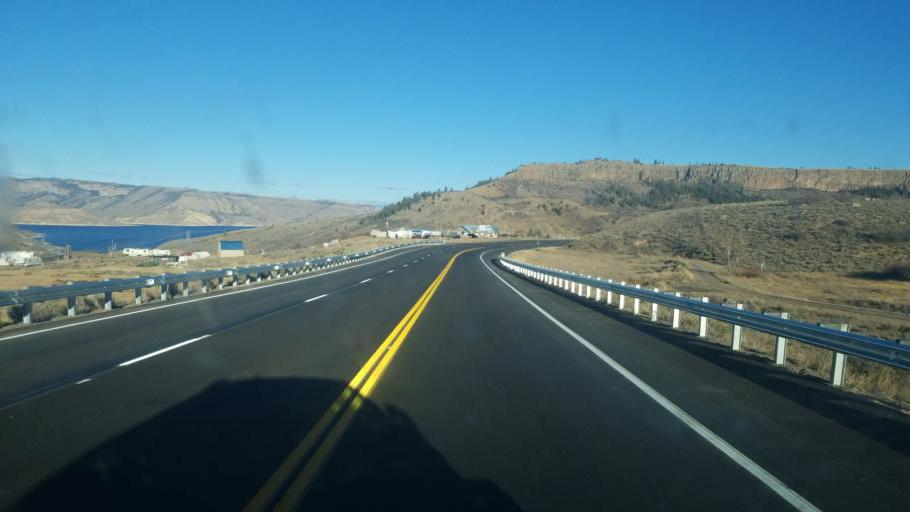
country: US
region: Colorado
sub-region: Hinsdale County
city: Lake City
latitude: 38.4407
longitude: -107.3525
